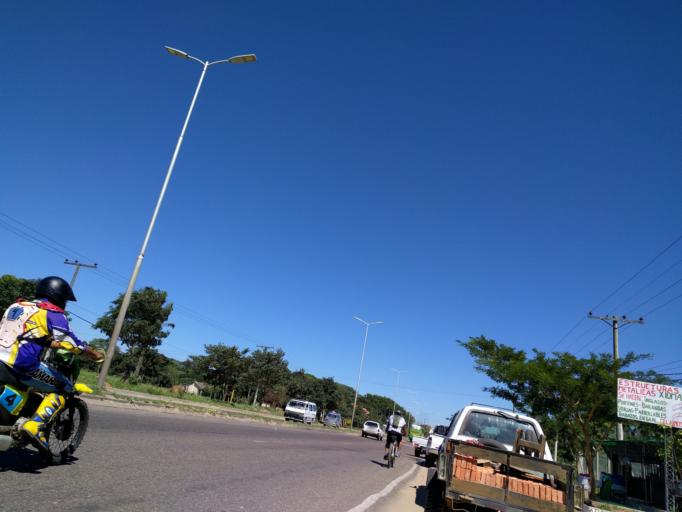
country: BO
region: Santa Cruz
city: Santa Cruz de la Sierra
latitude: -17.8649
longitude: -63.2683
